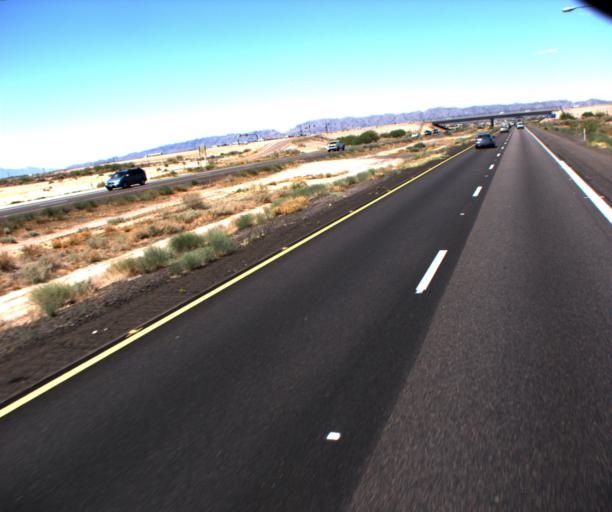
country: US
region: Arizona
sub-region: Maricopa County
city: Sun Lakes
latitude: 33.2523
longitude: -111.9455
